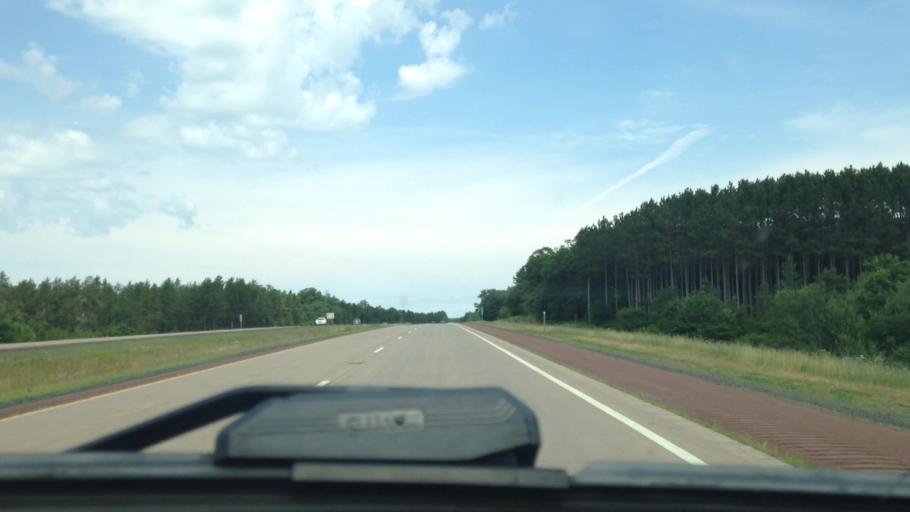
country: US
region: Wisconsin
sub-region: Douglas County
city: Lake Nebagamon
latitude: 46.3322
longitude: -91.8253
